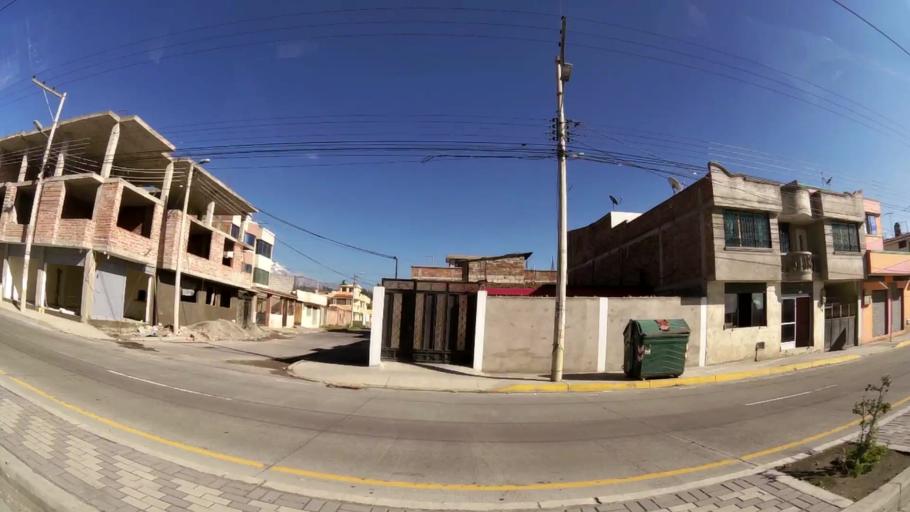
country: EC
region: Chimborazo
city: Riobamba
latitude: -1.6471
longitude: -78.6843
